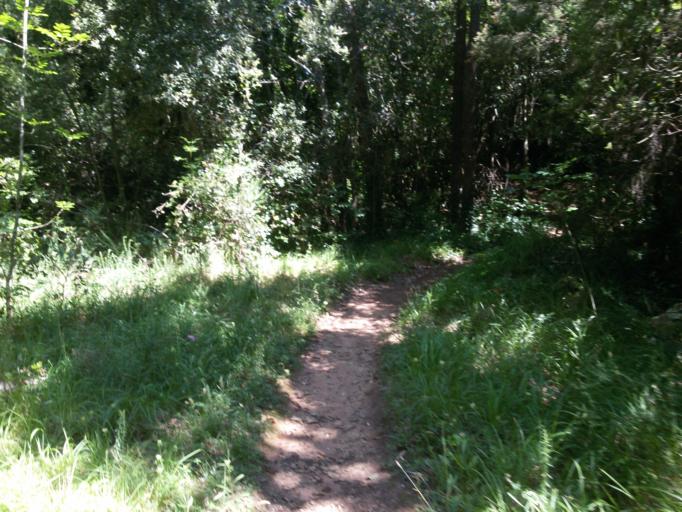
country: IT
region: Liguria
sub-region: Provincia di Savona
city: Borgio
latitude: 44.1720
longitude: 8.3170
